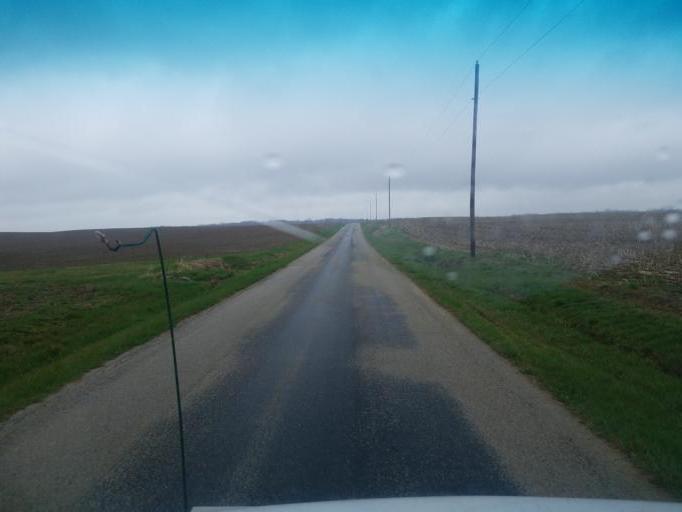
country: US
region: Ohio
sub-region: Huron County
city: Plymouth
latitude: 40.9649
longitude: -82.7217
